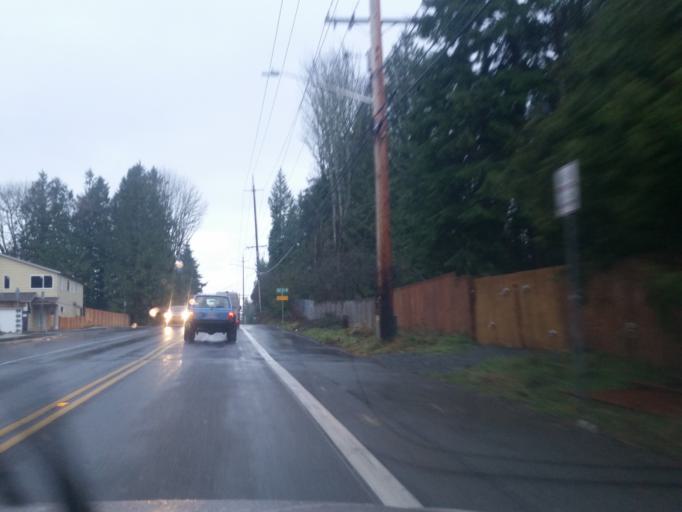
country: US
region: Washington
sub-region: Snohomish County
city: Meadowdale
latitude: 47.8716
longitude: -122.3009
